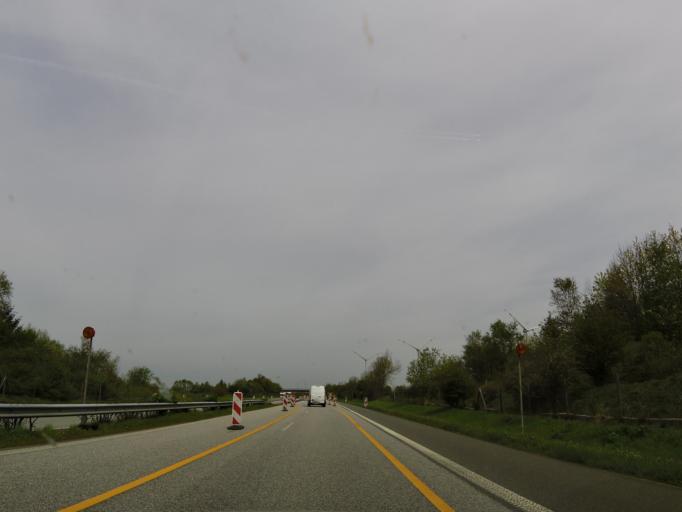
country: DE
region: Schleswig-Holstein
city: Tensbuttel-Rost
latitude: 54.0959
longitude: 9.2663
